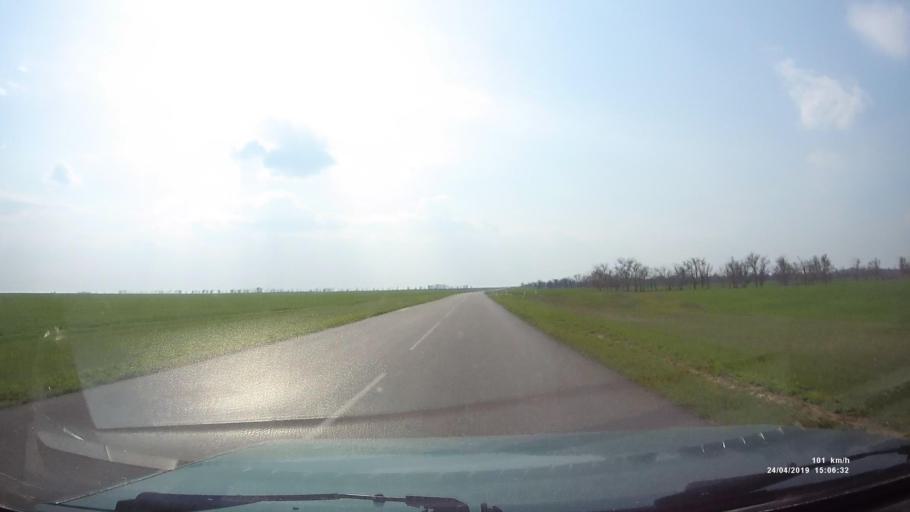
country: RU
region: Rostov
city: Remontnoye
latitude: 46.5588
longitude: 43.4250
